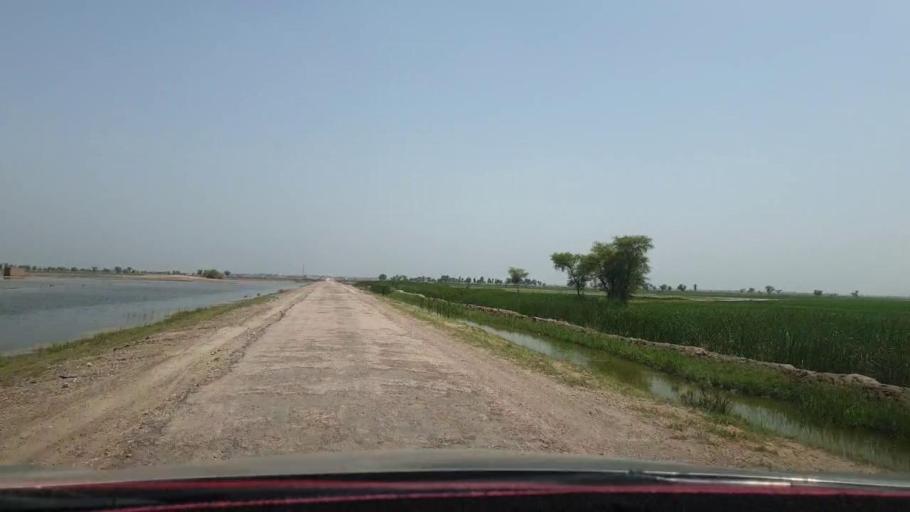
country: PK
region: Sindh
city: Warah
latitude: 27.3786
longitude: 67.7887
